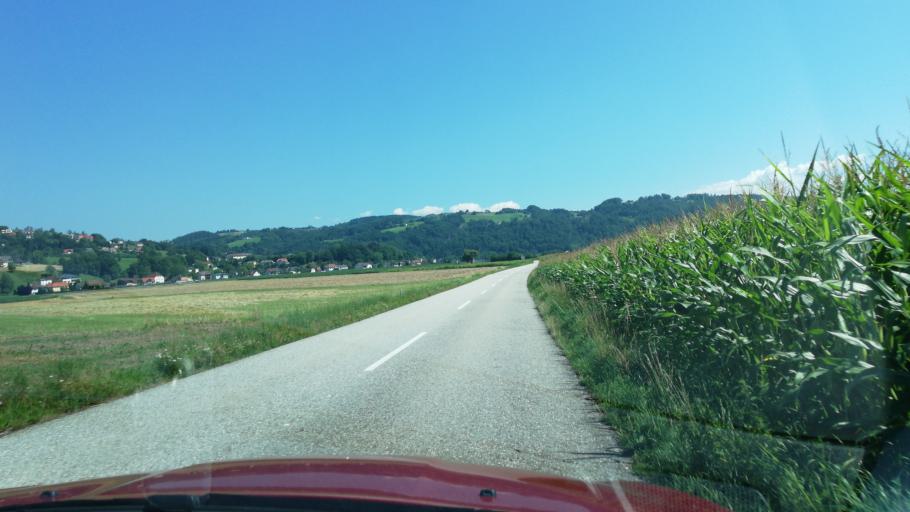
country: AT
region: Upper Austria
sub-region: Politischer Bezirk Urfahr-Umgebung
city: Feldkirchen an der Donau
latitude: 48.3509
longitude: 14.0542
